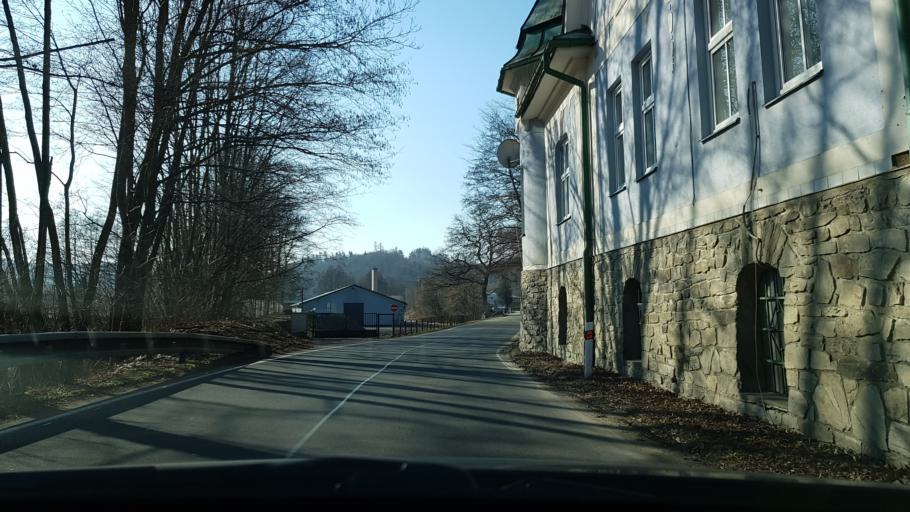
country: CZ
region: Olomoucky
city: Dolni Bohdikov
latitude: 50.0268
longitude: 16.8984
